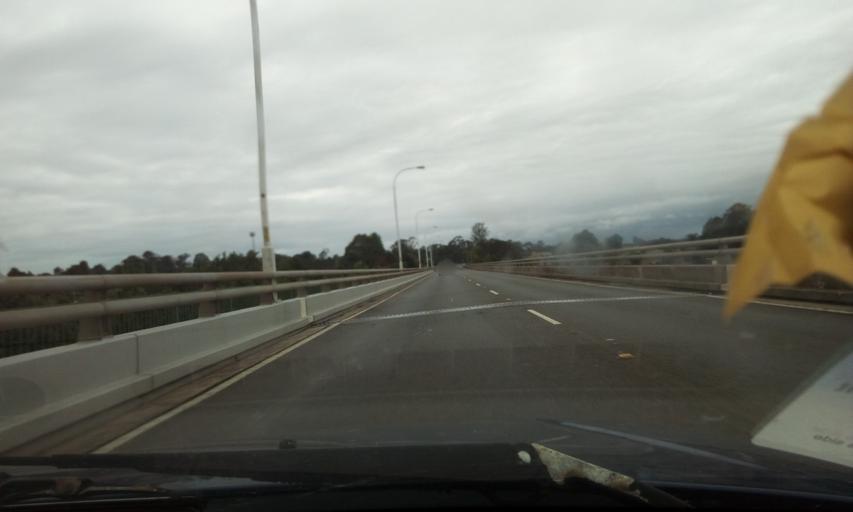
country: AU
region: New South Wales
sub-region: Camden
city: Camden South
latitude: -34.0681
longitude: 150.7070
